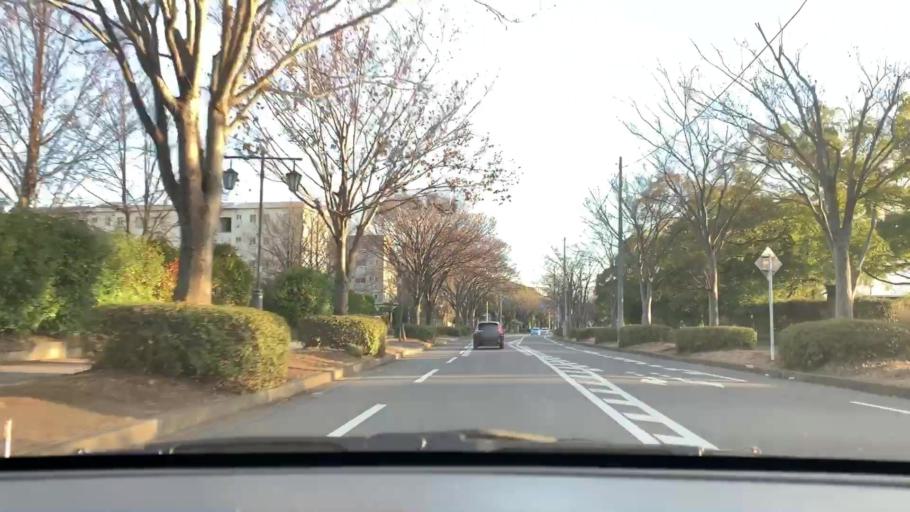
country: JP
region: Chiba
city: Kashiwa
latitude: 35.9002
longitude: 139.9395
